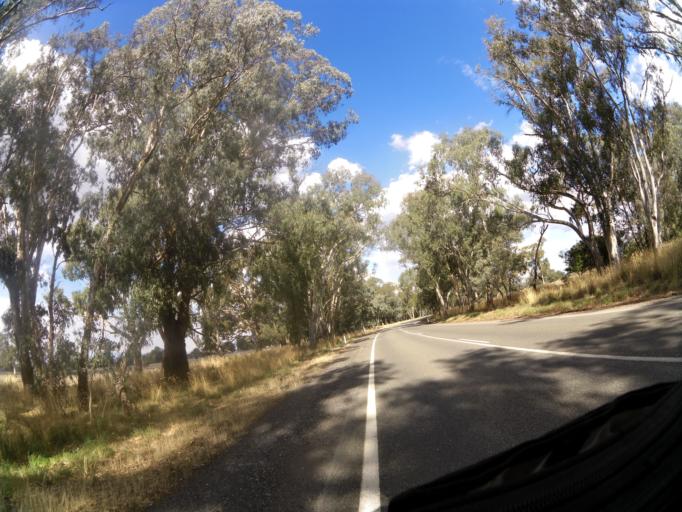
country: AU
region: Victoria
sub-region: Mansfield
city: Mansfield
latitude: -37.0032
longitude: 146.0772
